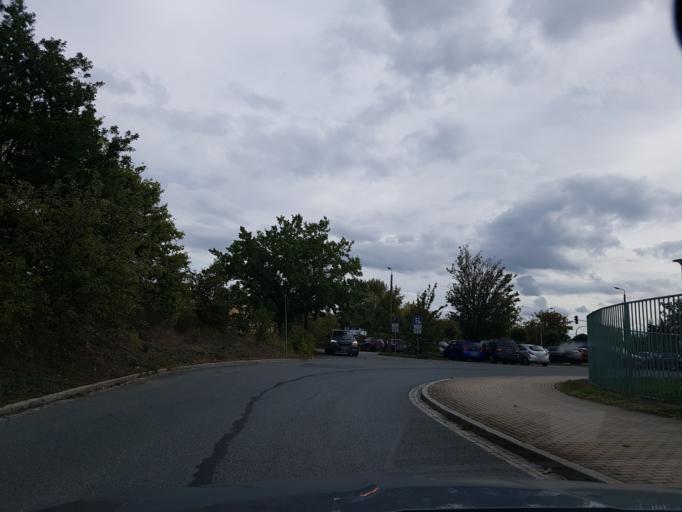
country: DE
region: Saxony
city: Riesa
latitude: 51.2948
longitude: 13.2948
